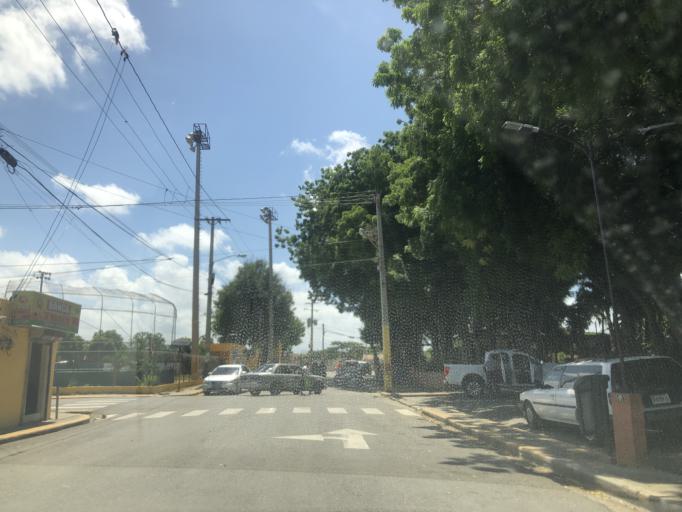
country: DO
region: Santiago
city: La Canela
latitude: 19.4511
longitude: -70.7788
